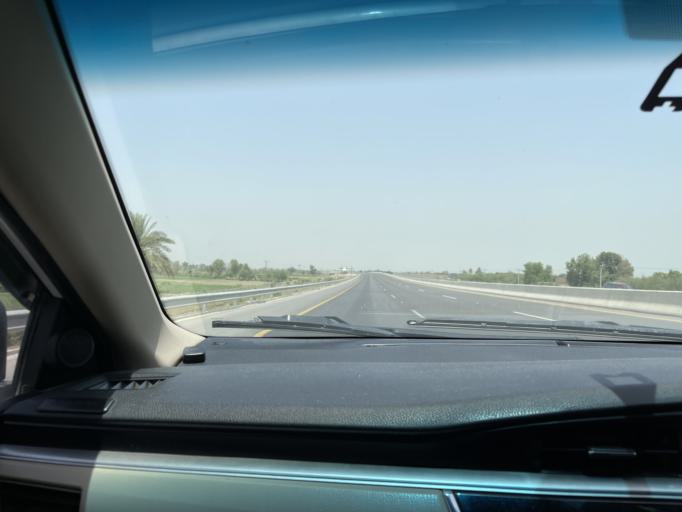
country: PK
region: Sindh
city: Ghotki
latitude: 28.0181
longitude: 69.2885
